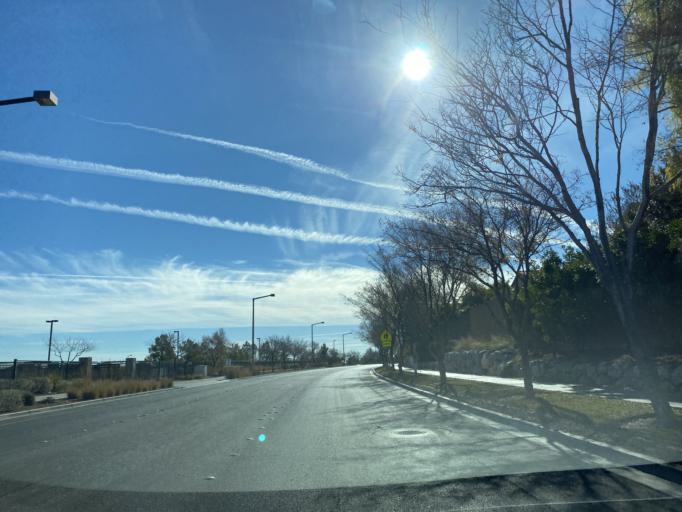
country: US
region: Nevada
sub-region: Clark County
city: Summerlin South
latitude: 36.1542
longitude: -115.3189
